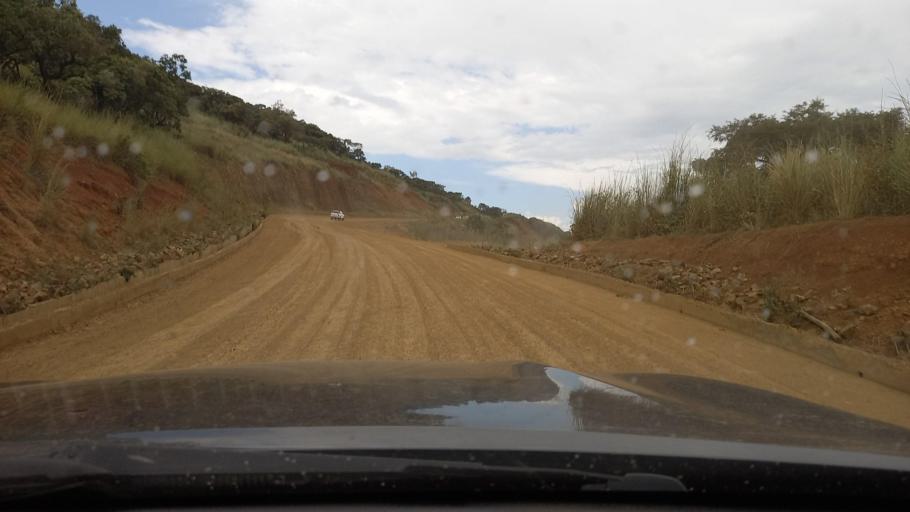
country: ET
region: Southern Nations, Nationalities, and People's Region
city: Mizan Teferi
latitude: 6.2013
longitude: 35.6602
